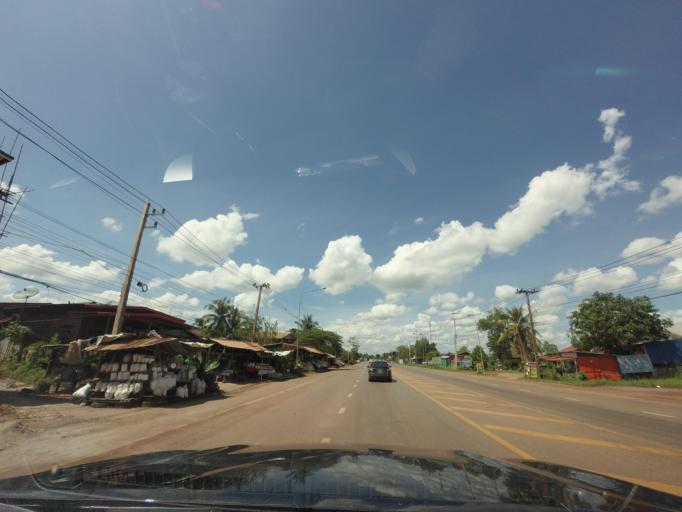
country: TH
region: Changwat Udon Thani
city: Ban Dung
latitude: 17.7060
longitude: 103.2515
